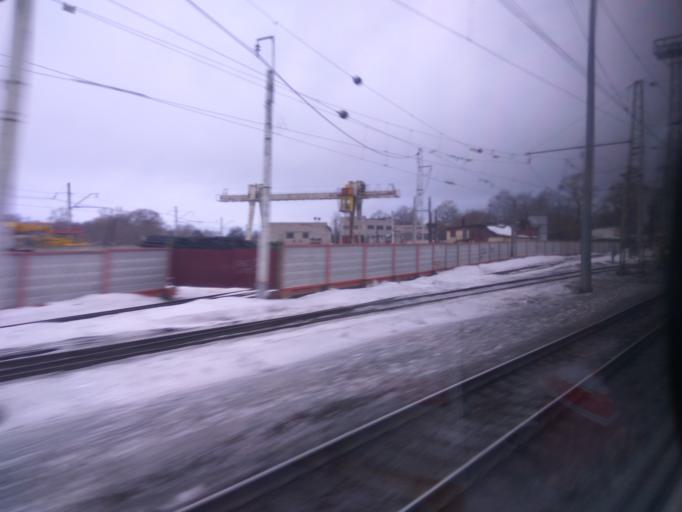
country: RU
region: Tverskaya
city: Tver
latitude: 56.8325
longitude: 35.8997
